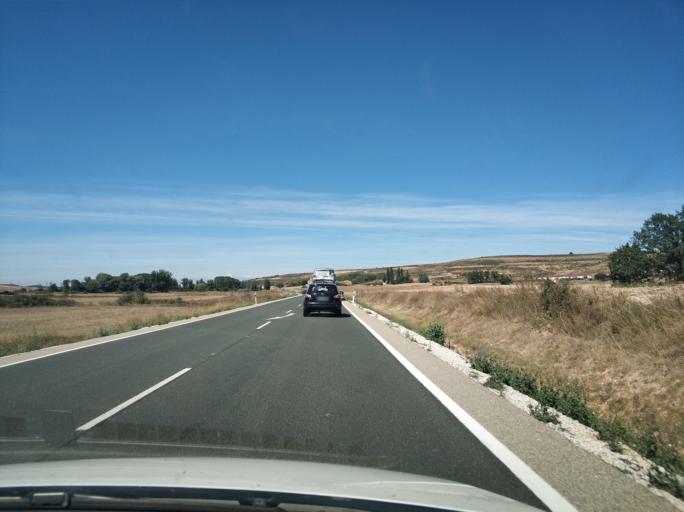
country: ES
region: Castille and Leon
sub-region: Provincia de Burgos
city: Tubilla del Agua
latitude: 42.6394
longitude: -3.8747
